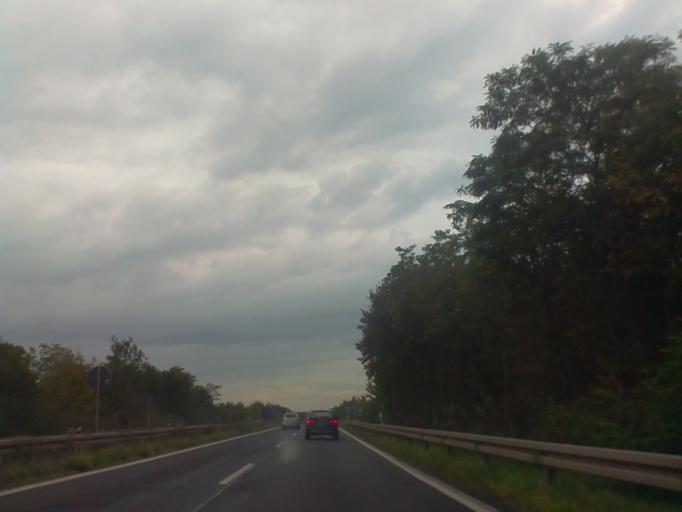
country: DE
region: Bavaria
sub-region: Regierungsbezirk Unterfranken
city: Kleinostheim
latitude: 49.9913
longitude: 9.0518
